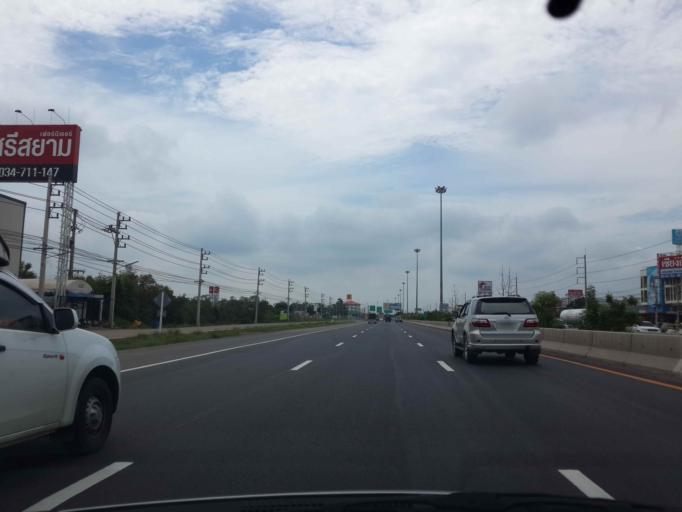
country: TH
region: Samut Songkhram
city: Samut Songkhram
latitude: 13.4057
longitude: 100.0155
